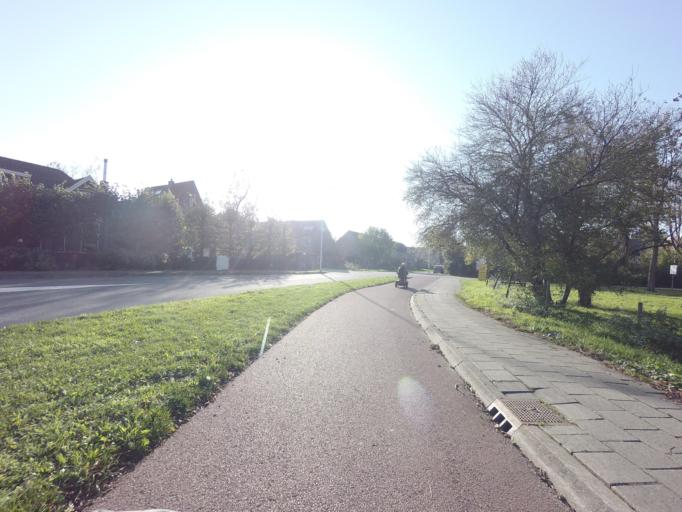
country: NL
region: South Holland
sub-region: Bodegraven-Reeuwijk
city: Bodegraven
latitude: 52.1058
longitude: 4.7241
